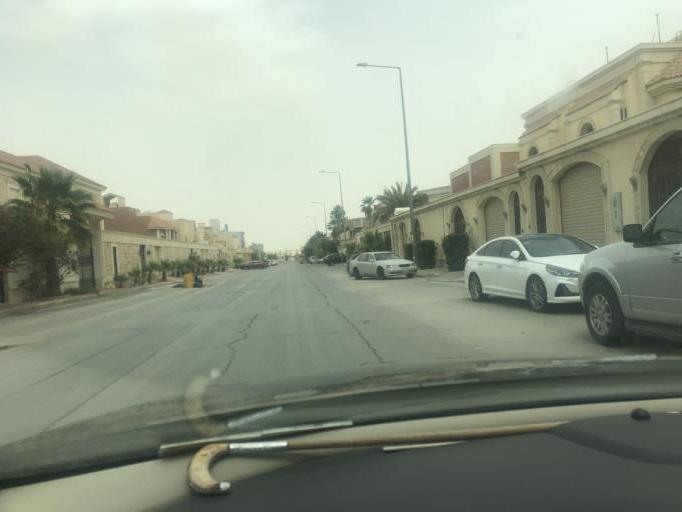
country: SA
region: Ar Riyad
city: Riyadh
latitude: 24.7351
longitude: 46.7859
